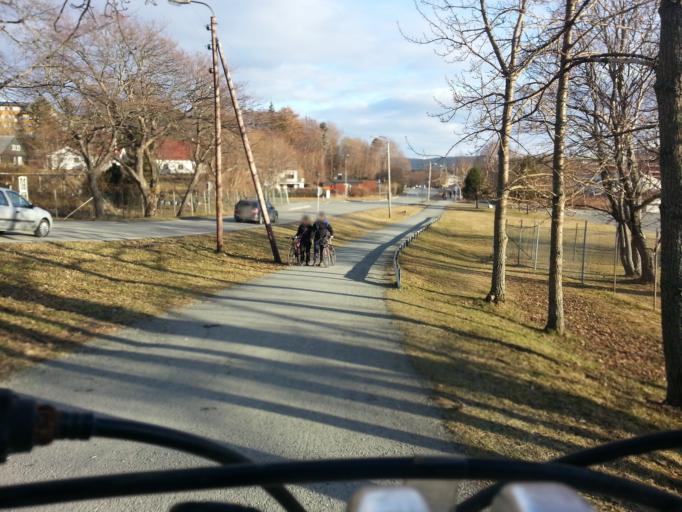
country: NO
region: Sor-Trondelag
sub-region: Trondheim
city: Trondheim
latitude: 63.4461
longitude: 10.4539
